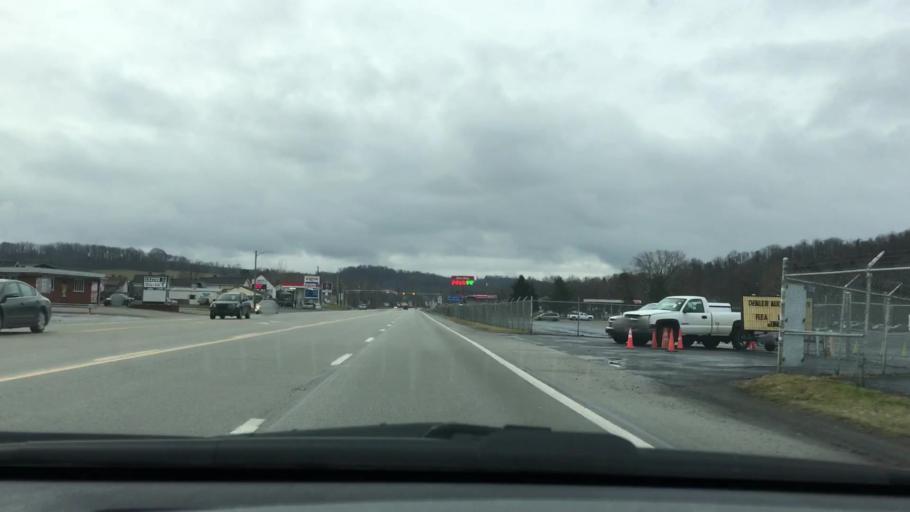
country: US
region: Pennsylvania
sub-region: Fayette County
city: Perryopolis
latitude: 40.0890
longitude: -79.7612
